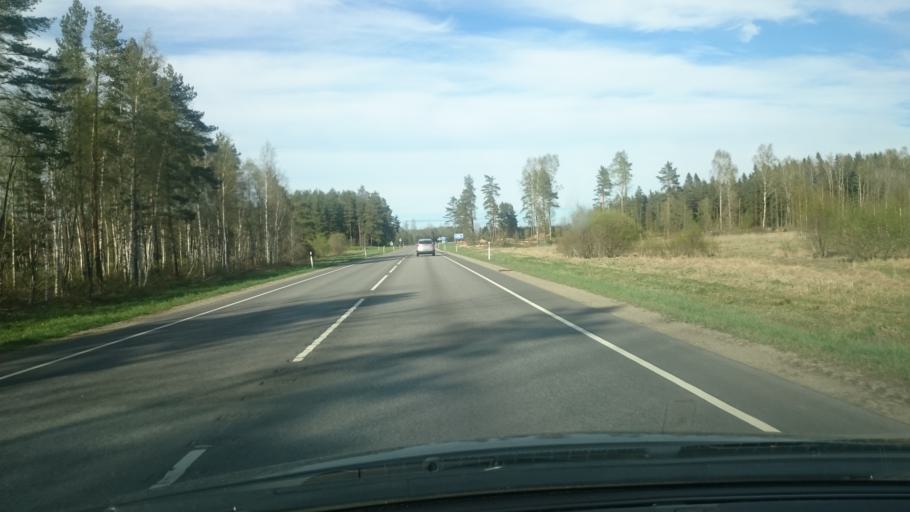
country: EE
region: Ida-Virumaa
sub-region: Toila vald
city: Voka
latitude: 59.3864
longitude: 27.5727
